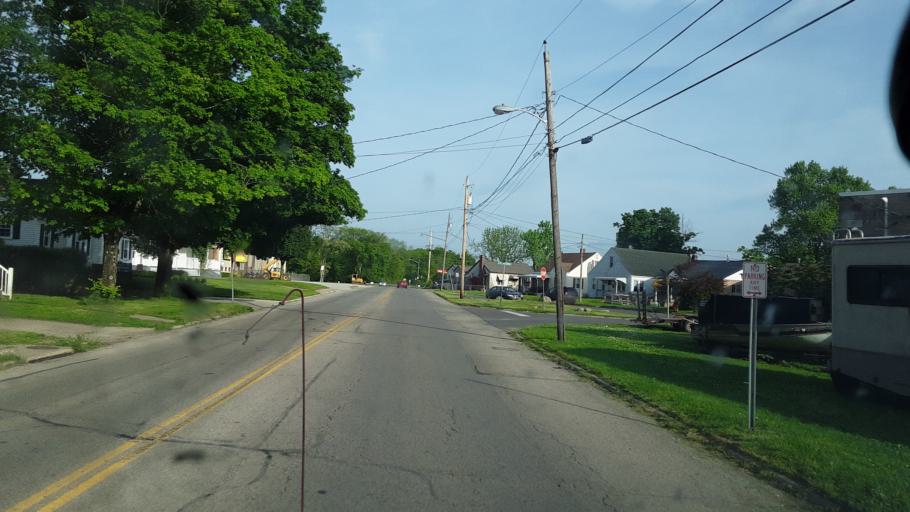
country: US
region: Ohio
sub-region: Pickaway County
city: Circleville
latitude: 39.5969
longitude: -82.9312
